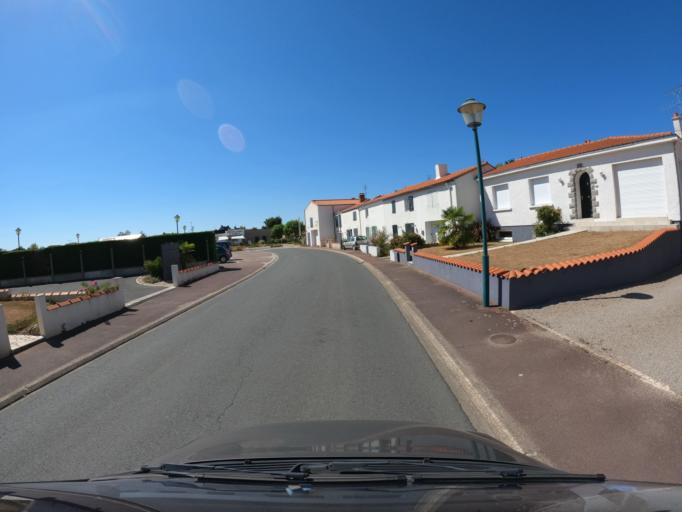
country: FR
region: Pays de la Loire
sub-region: Departement de la Vendee
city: La Boissiere-de-Montaigu
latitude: 46.9502
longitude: -1.1893
